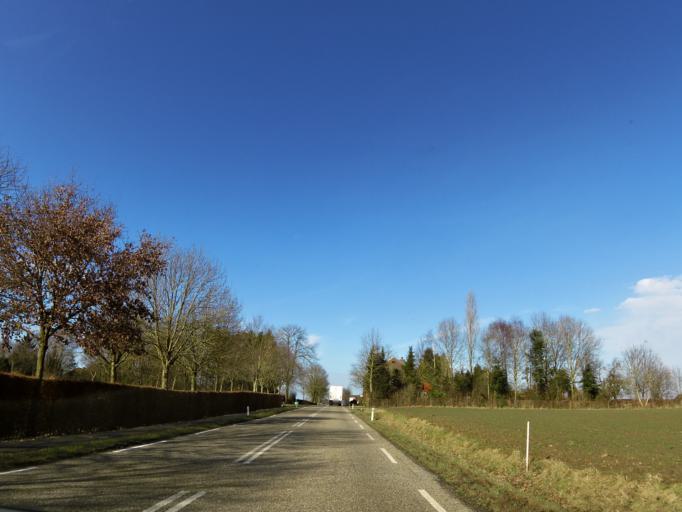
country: NL
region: Limburg
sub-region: Eijsden-Margraten
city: Margraten
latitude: 50.7837
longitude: 5.8343
